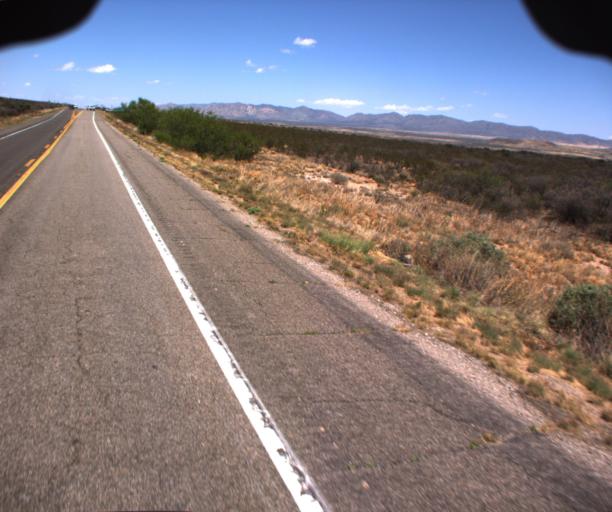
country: US
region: Arizona
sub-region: Cochise County
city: Tombstone
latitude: 31.6706
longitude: -110.0319
